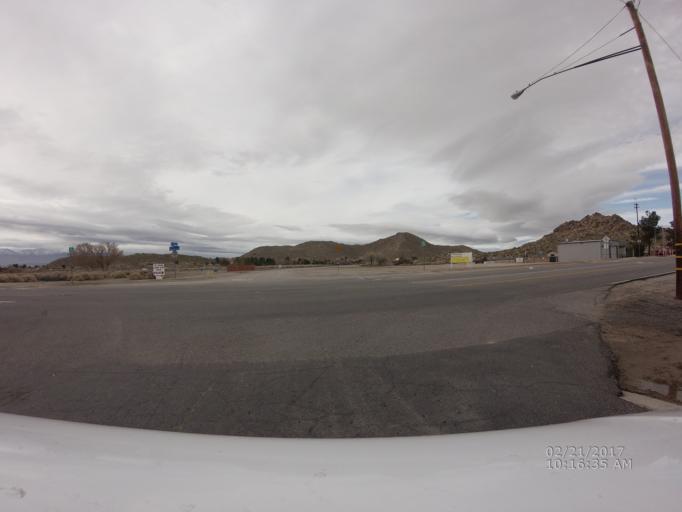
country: US
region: California
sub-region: Los Angeles County
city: Lake Los Angeles
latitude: 34.6064
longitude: -117.8245
